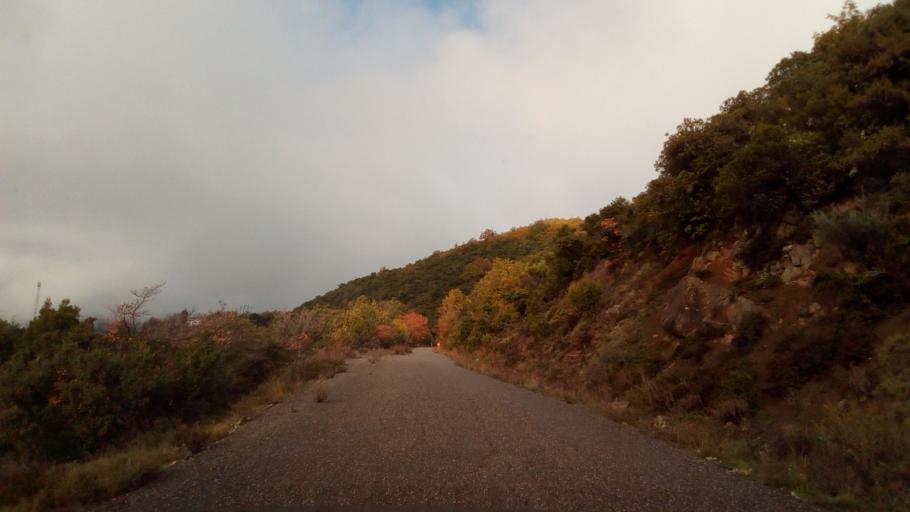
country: GR
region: West Greece
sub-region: Nomos Aitolias kai Akarnanias
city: Nafpaktos
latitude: 38.5182
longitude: 21.9477
